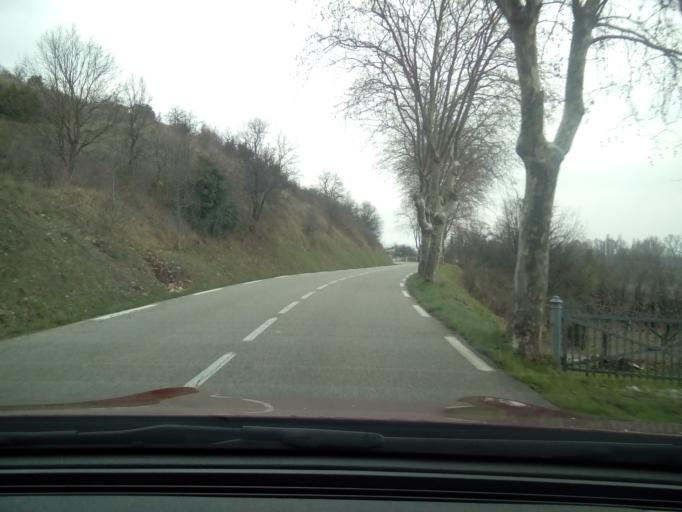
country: FR
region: Rhone-Alpes
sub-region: Departement de la Drome
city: Saulce-sur-Rhone
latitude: 44.7059
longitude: 4.7647
